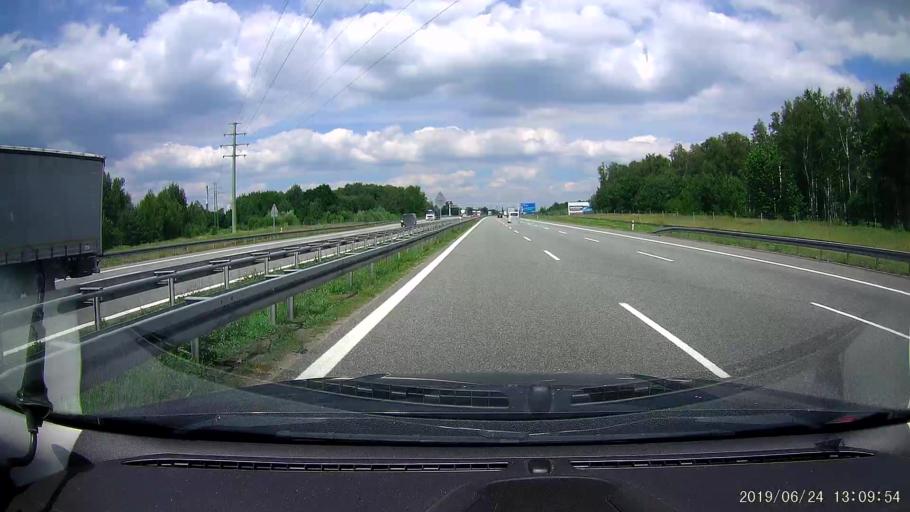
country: PL
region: Silesian Voivodeship
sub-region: Powiat gliwicki
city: Gieraltowice
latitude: 50.2074
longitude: 18.6959
